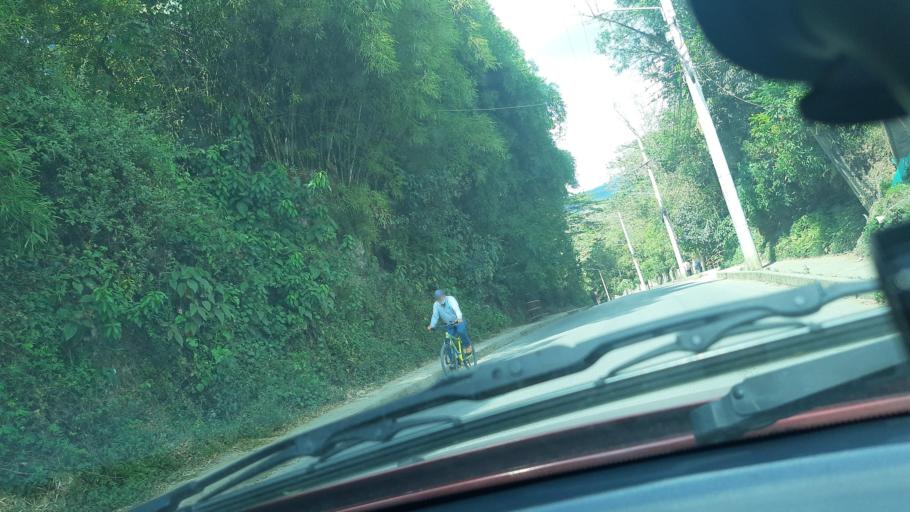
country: CO
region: Boyaca
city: Moniquira
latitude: 5.8703
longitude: -73.5739
